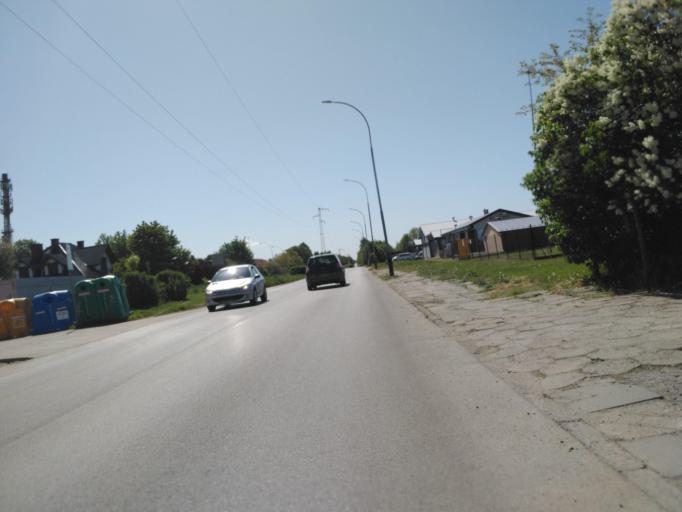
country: PL
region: Subcarpathian Voivodeship
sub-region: Krosno
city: Krosno
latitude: 49.6798
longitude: 21.7809
